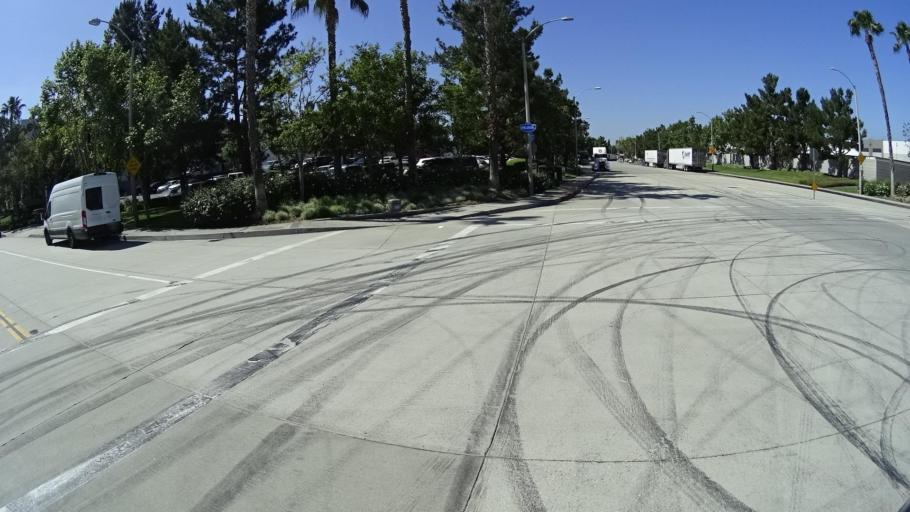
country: US
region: California
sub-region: Los Angeles County
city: Walnut
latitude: 34.0114
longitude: -117.8372
